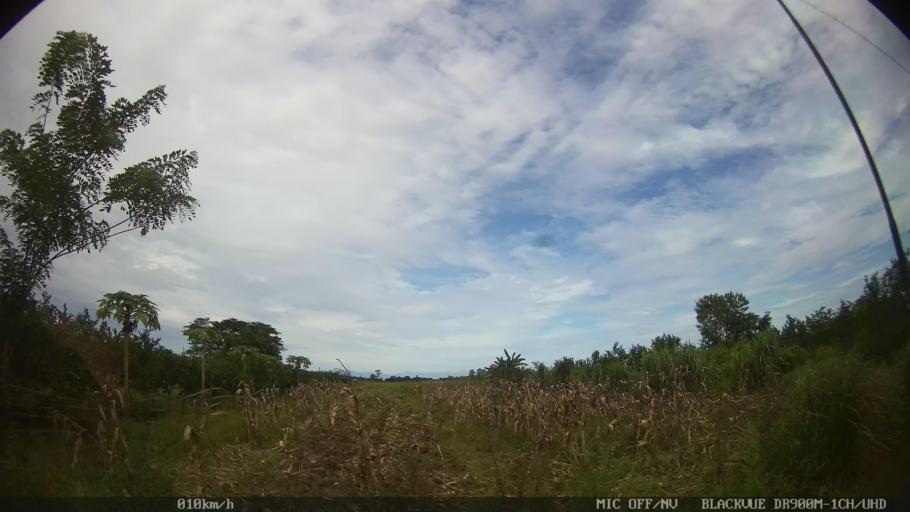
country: ID
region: North Sumatra
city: Sunggal
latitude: 3.5780
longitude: 98.5772
